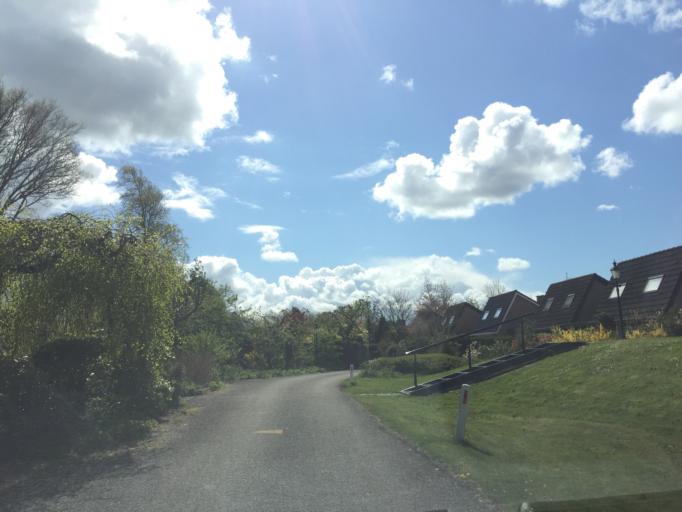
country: NL
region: South Holland
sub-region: Gemeente Leiderdorp
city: Leiderdorp
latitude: 52.1864
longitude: 4.5419
